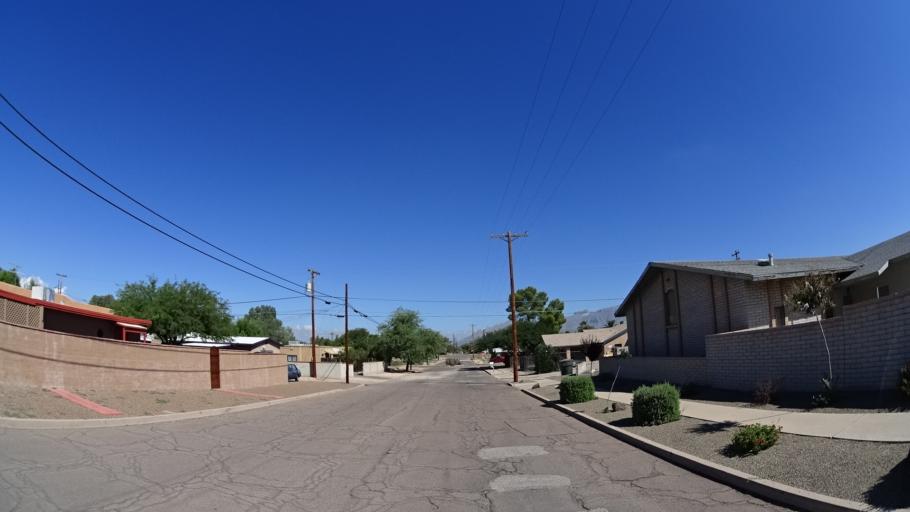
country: US
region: Arizona
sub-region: Pima County
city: Tucson
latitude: 32.2480
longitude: -110.9554
